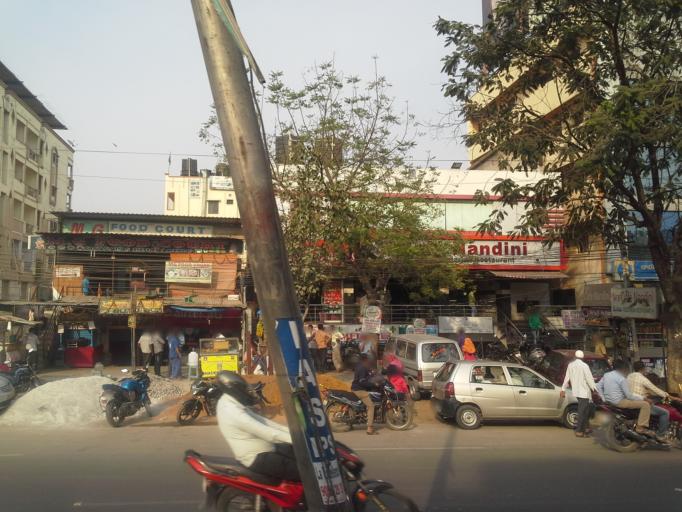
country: IN
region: Telangana
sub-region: Rangareddi
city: Kukatpalli
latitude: 17.4413
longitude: 78.3598
